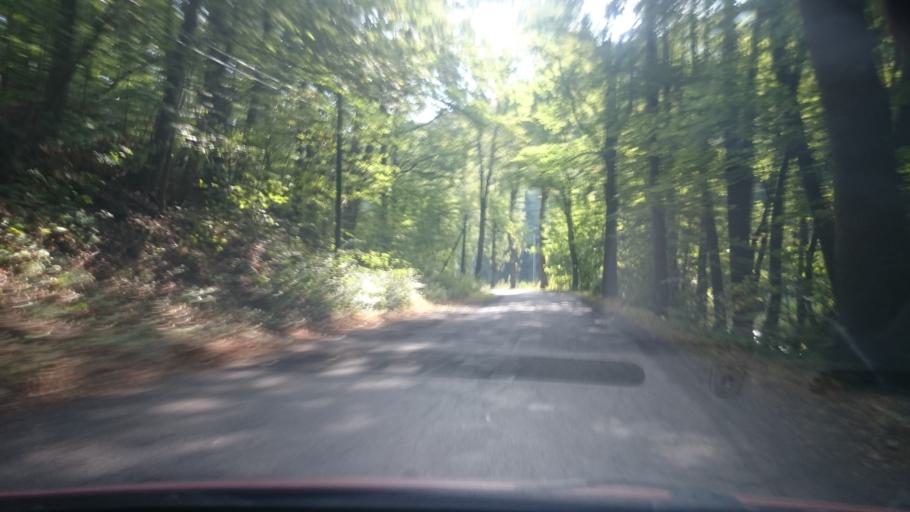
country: PL
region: Lower Silesian Voivodeship
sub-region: Powiat klodzki
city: Bystrzyca Klodzka
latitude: 50.3019
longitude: 16.5707
